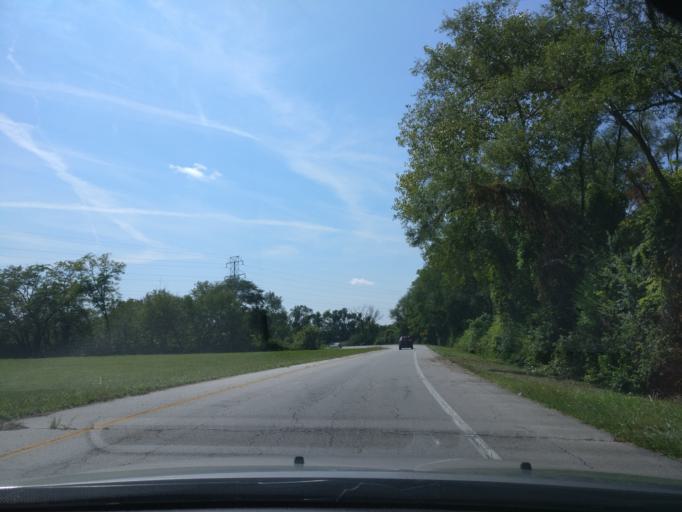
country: US
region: Ohio
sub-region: Butler County
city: Middletown
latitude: 39.4854
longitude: -84.4149
